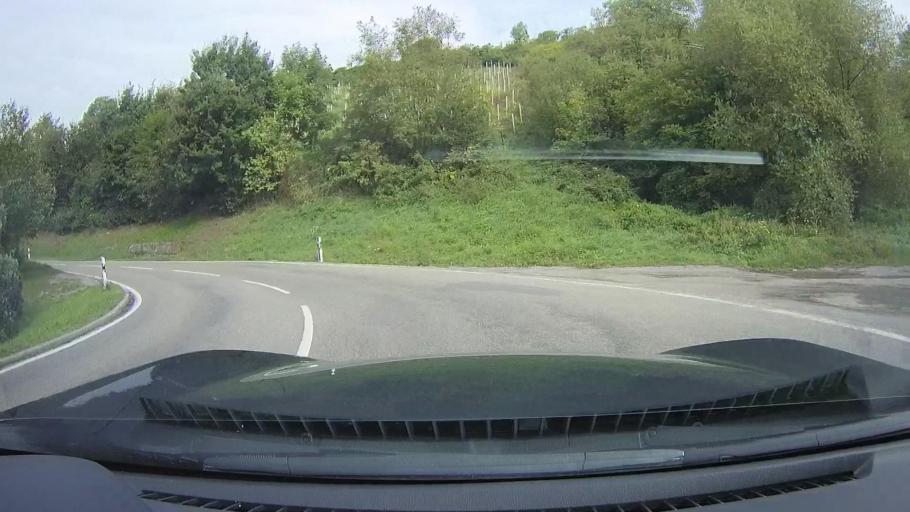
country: DE
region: Baden-Wuerttemberg
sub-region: Regierungsbezirk Stuttgart
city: Lowenstein
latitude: 49.0902
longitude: 9.3823
